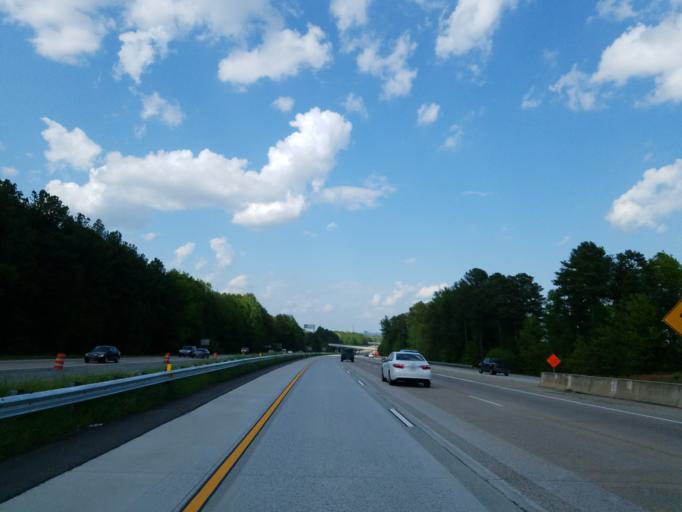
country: US
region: Georgia
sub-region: Forsyth County
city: Cumming
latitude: 34.1880
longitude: -84.1351
